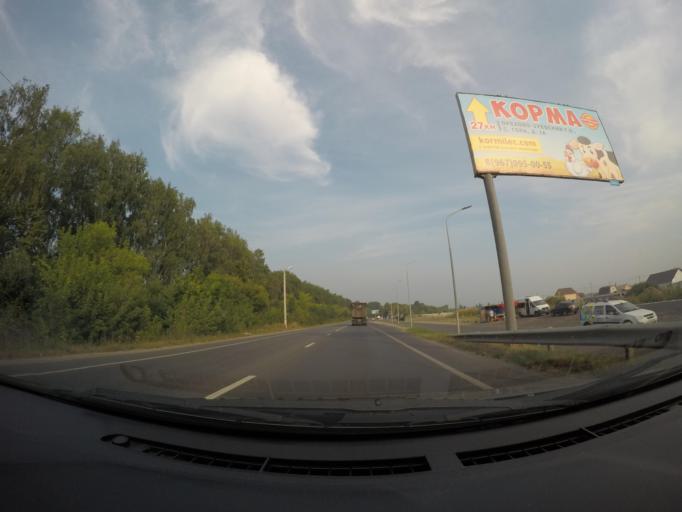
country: RU
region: Moskovskaya
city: Rechitsy
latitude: 55.5890
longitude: 38.5305
